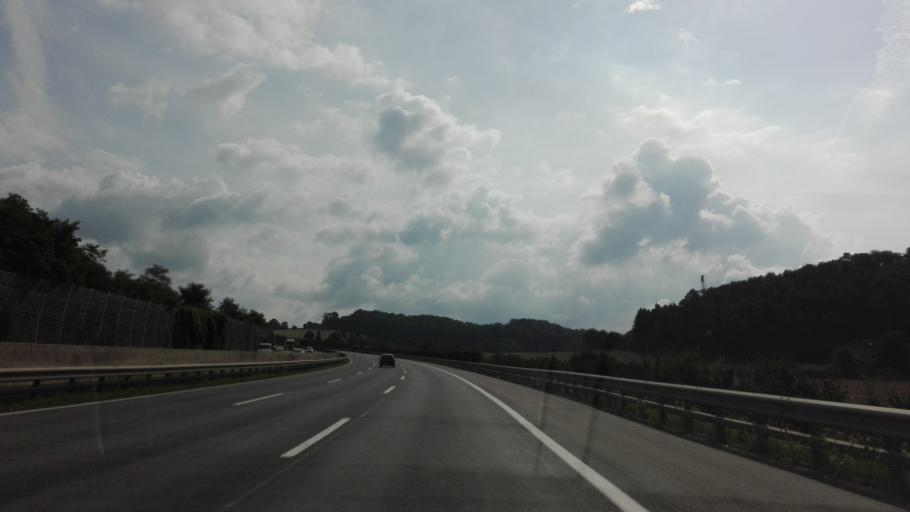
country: AT
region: Lower Austria
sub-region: Politischer Bezirk Melk
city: Melk
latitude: 48.2140
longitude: 15.3099
